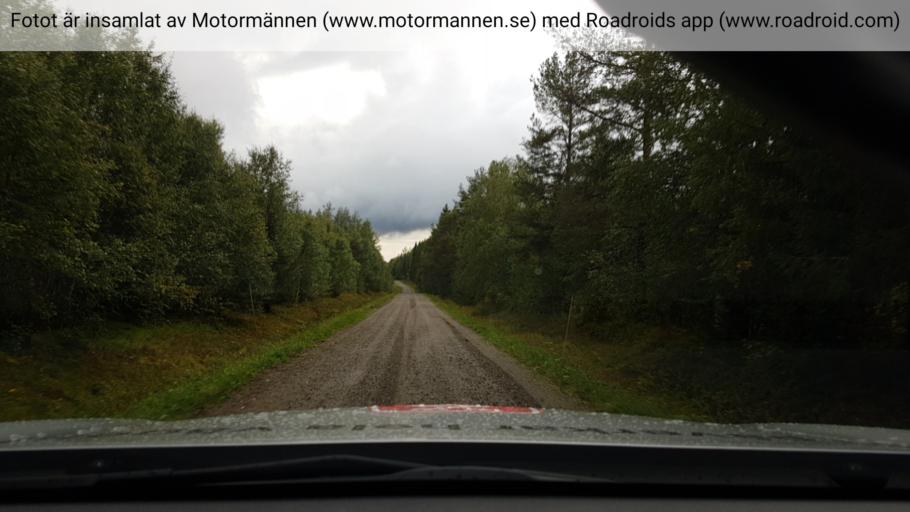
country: SE
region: Vaesterbotten
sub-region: Asele Kommun
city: Asele
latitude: 64.1435
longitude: 16.8989
